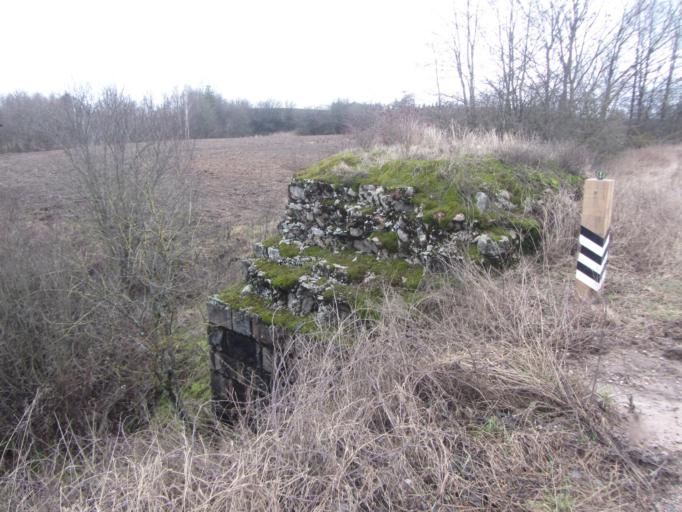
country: LT
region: Alytaus apskritis
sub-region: Alytus
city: Alytus
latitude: 54.3575
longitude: 24.1795
